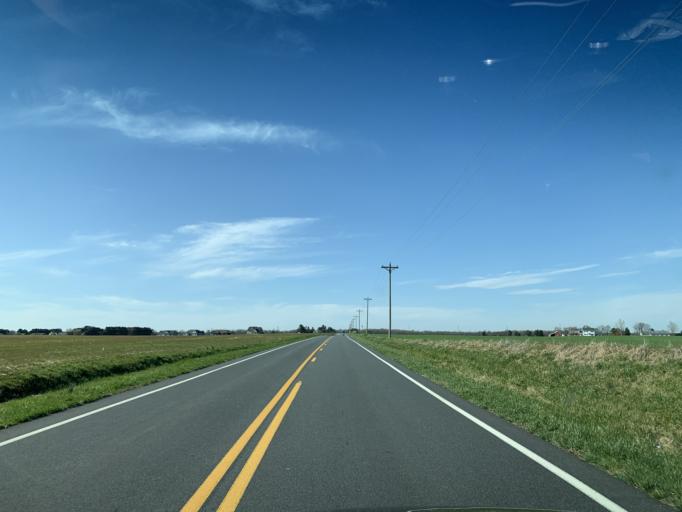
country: US
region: Delaware
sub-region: Kent County
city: Riverview
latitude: 38.9935
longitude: -75.5155
